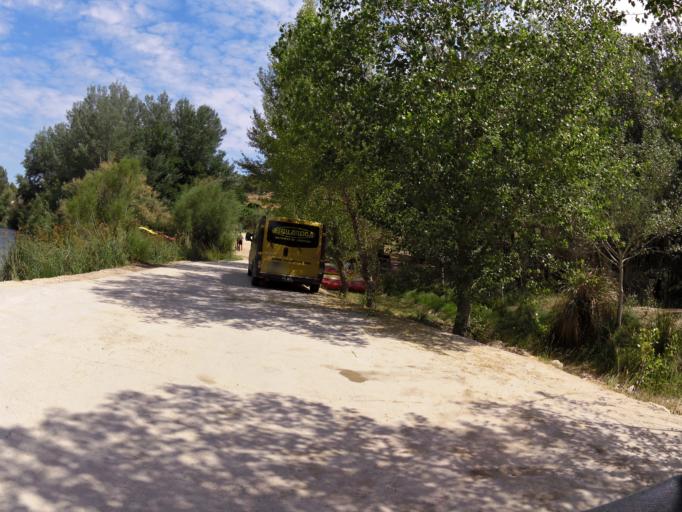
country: ES
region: Castille-La Mancha
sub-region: Provincia de Albacete
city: Casas Ibanez
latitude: 39.3690
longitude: -1.4487
